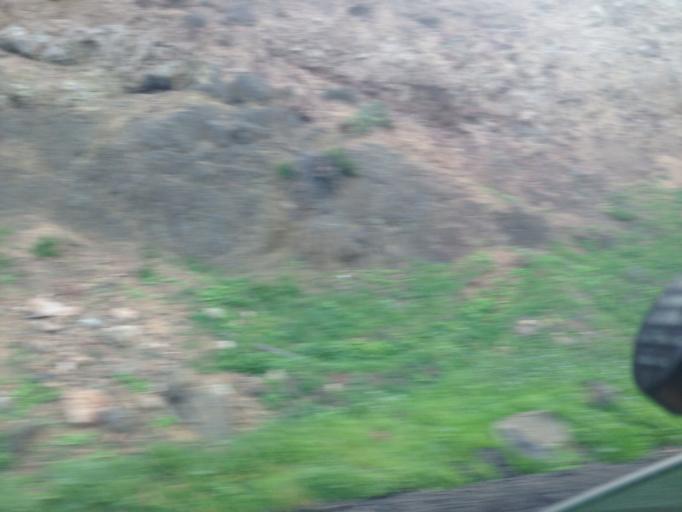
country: MX
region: Baja California
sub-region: Playas de Rosarito
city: Santa Anita
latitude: 32.1122
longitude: -116.8834
